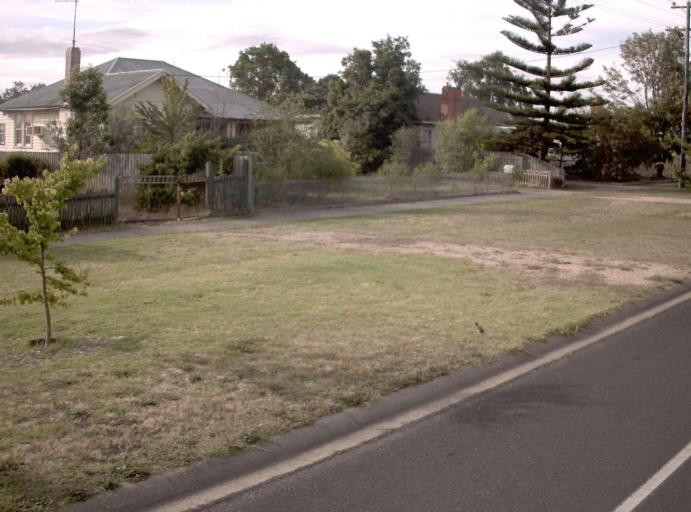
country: AU
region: Victoria
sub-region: Wellington
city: Sale
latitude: -37.9664
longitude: 146.9850
